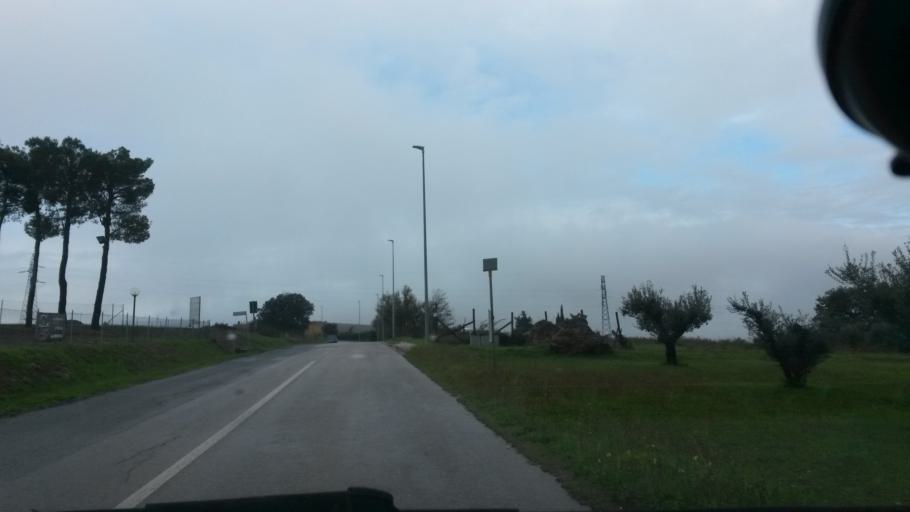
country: IT
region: Tuscany
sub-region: Provincia di Livorno
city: Rosignano Marittimo
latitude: 43.4158
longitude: 10.4631
